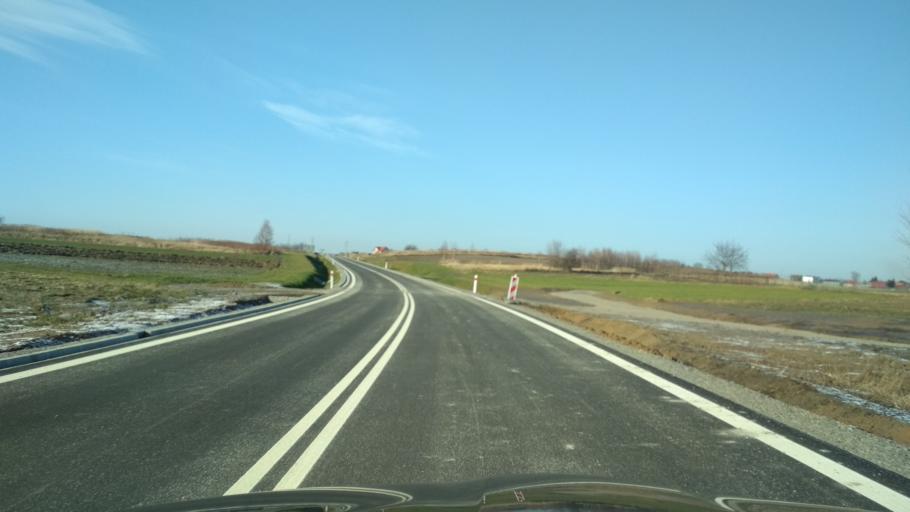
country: PL
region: Subcarpathian Voivodeship
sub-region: Powiat ropczycko-sedziszowski
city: Sedziszow Malopolski
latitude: 50.0732
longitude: 21.7311
